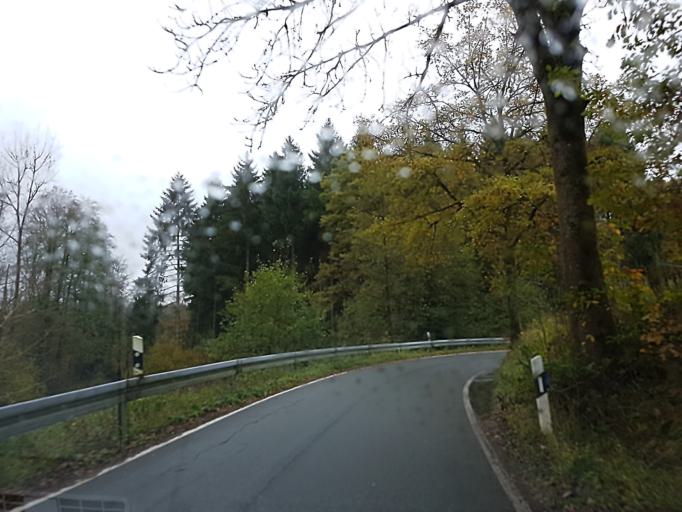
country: DE
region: North Rhine-Westphalia
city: Kierspe
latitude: 51.0910
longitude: 7.5783
